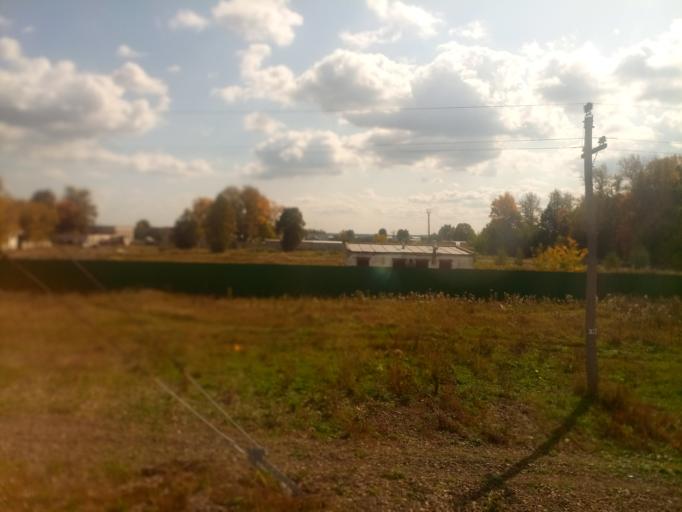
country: RU
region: Chuvashia
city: Urmary
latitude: 55.6881
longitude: 47.9488
